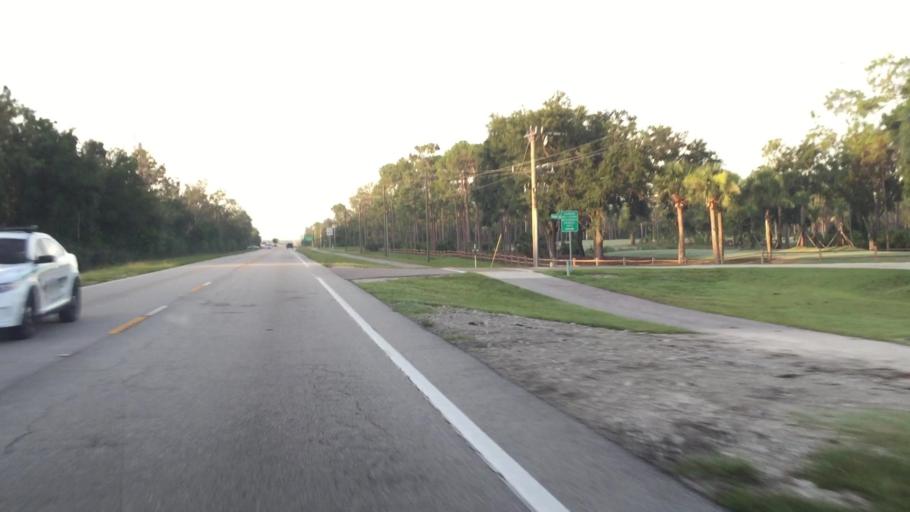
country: US
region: Florida
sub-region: Lee County
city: Fort Myers
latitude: 26.6232
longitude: -81.8116
